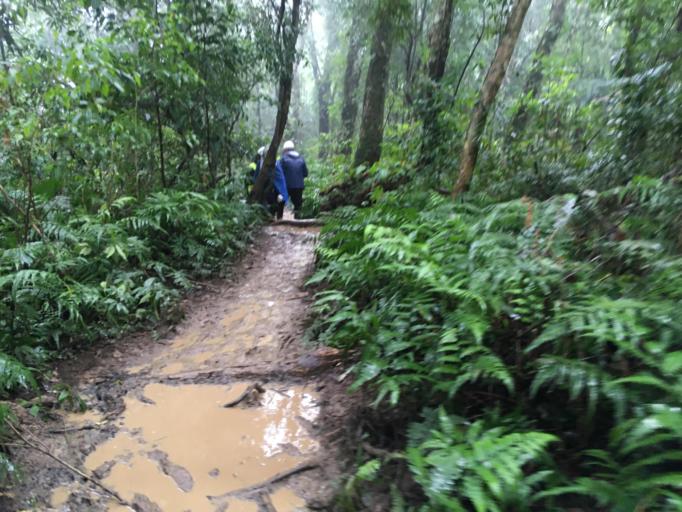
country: TW
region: Taiwan
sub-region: Yilan
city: Yilan
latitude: 24.6784
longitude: 121.5684
